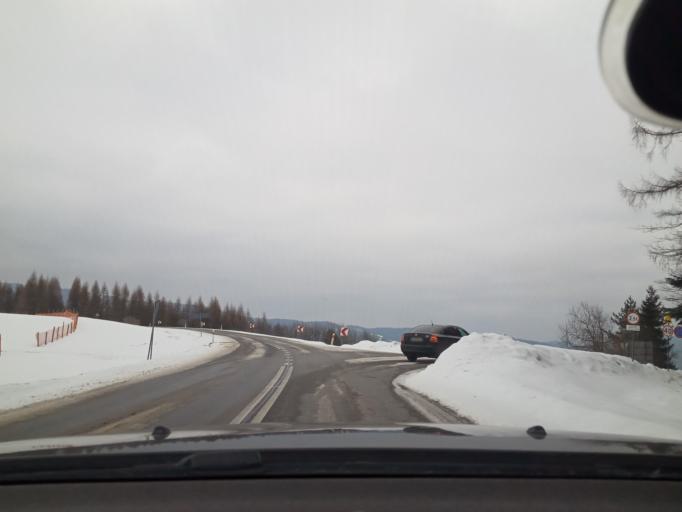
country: PL
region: Lesser Poland Voivodeship
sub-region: Powiat nowotarski
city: Krosnica
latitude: 49.4281
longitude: 20.3510
